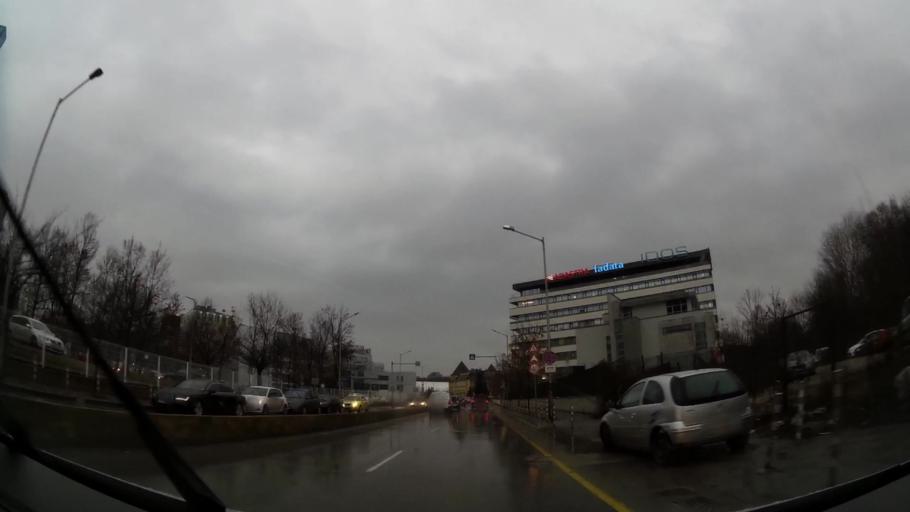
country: BG
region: Sofia-Capital
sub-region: Stolichna Obshtina
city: Sofia
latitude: 42.6645
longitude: 23.3260
